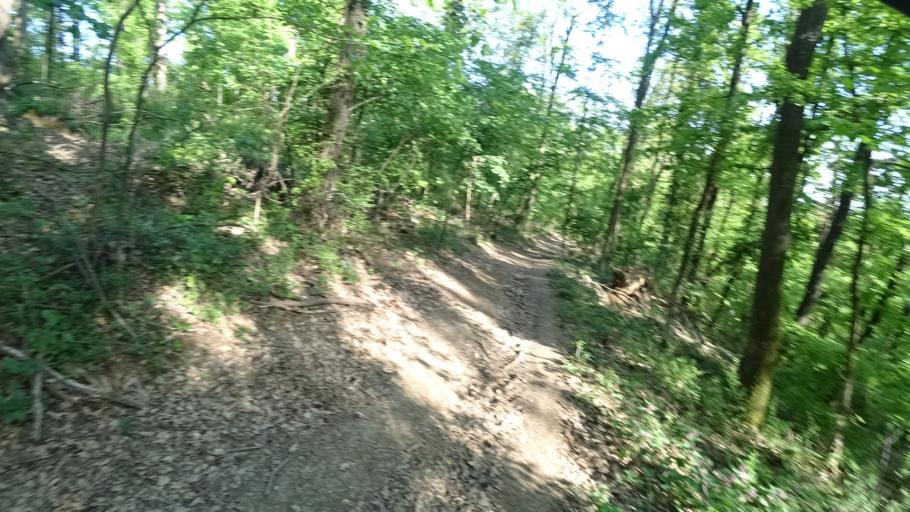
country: HR
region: Grad Zagreb
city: Stenjevec
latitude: 45.8462
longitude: 15.9168
